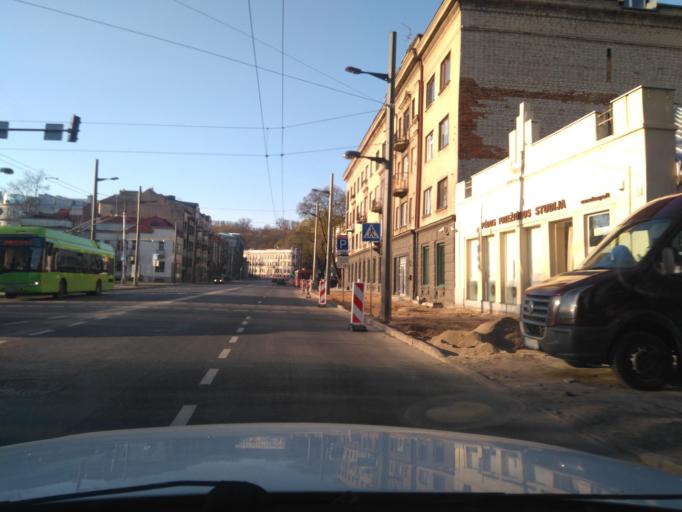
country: LT
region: Kauno apskritis
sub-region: Kaunas
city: Kaunas
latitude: 54.8950
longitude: 23.9252
